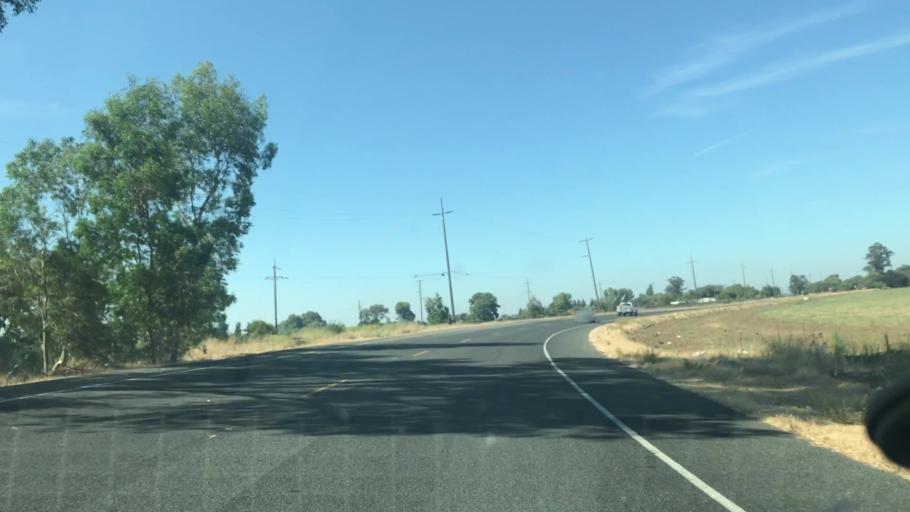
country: US
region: California
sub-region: Solano County
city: Vacaville
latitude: 38.3426
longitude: -121.9154
